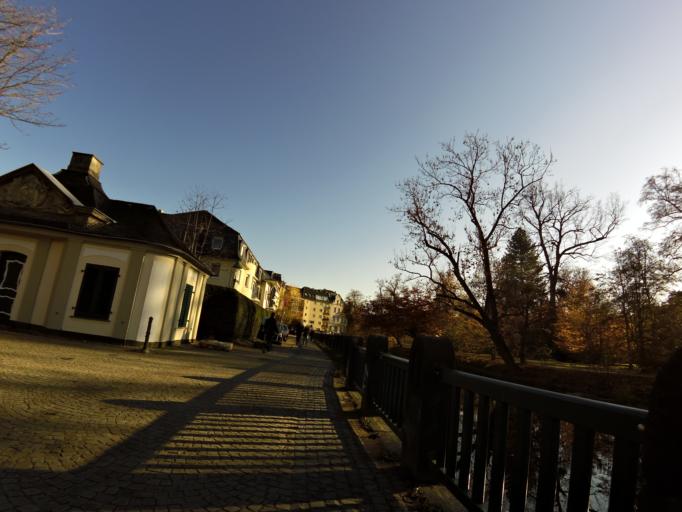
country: DE
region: North Rhine-Westphalia
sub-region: Regierungsbezirk Koln
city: Bonn
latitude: 50.7260
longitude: 7.0939
